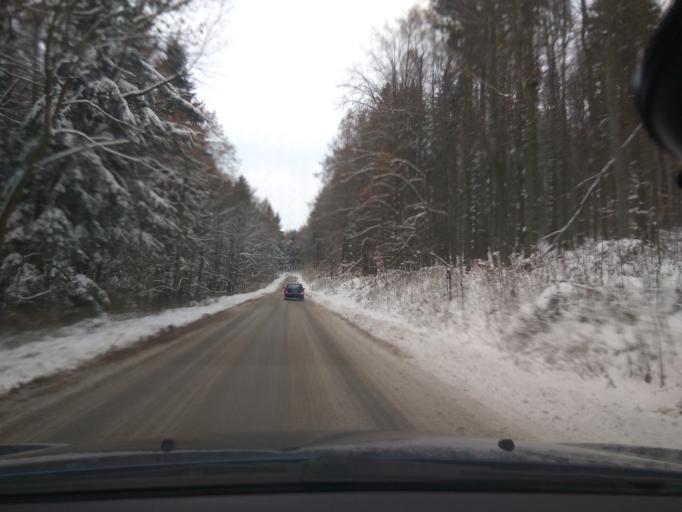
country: CZ
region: Zlin
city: Strani
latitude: 48.8488
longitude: 17.6881
